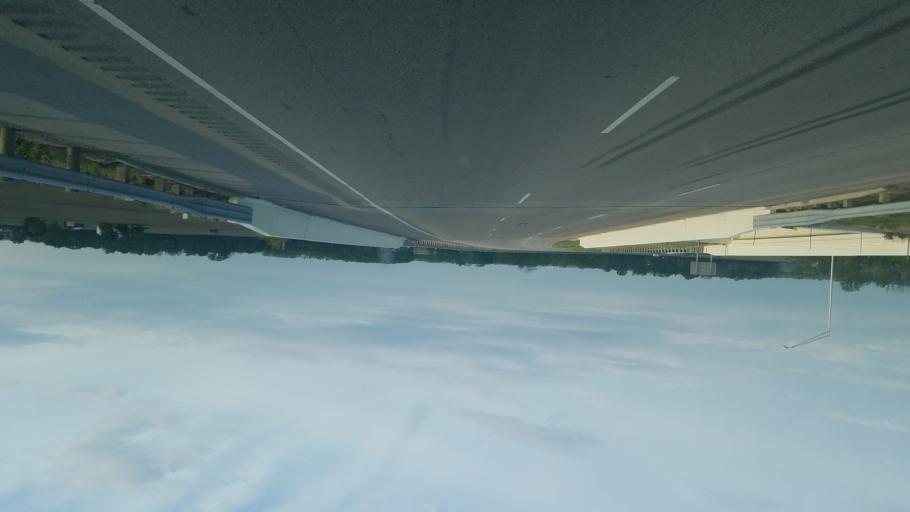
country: US
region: Ohio
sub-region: Clinton County
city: Wilmington
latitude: 39.4595
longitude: -83.7764
